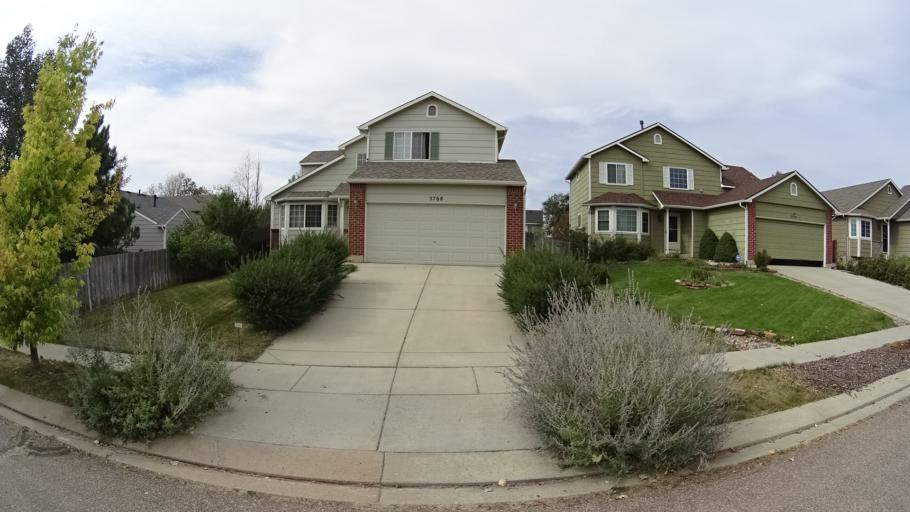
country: US
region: Colorado
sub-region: El Paso County
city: Cimarron Hills
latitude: 38.9151
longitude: -104.7150
